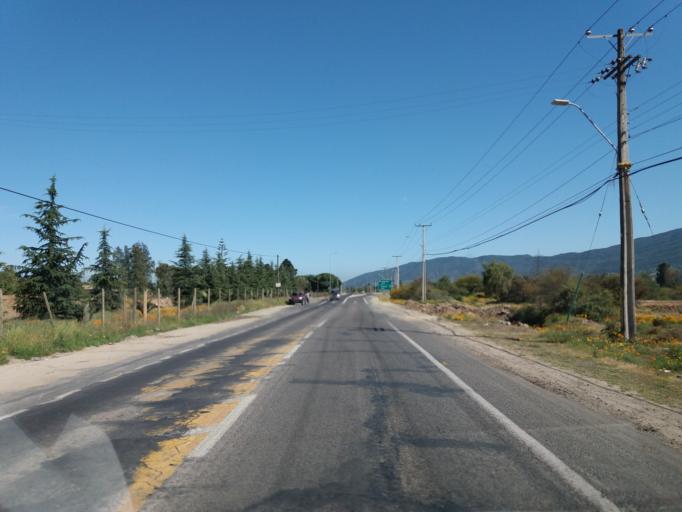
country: CL
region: Valparaiso
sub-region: Provincia de Marga Marga
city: Limache
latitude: -33.0216
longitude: -71.1678
